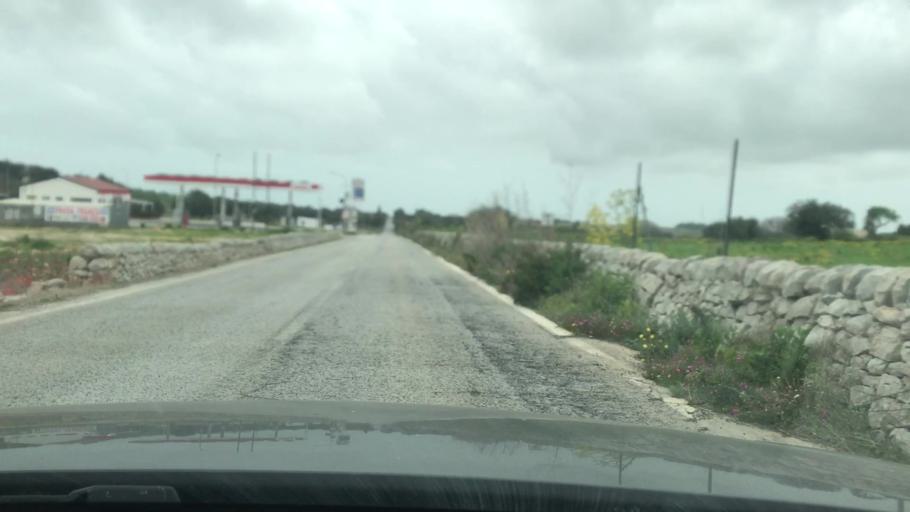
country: IT
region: Sicily
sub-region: Ragusa
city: Scicli
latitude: 36.8139
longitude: 14.7325
